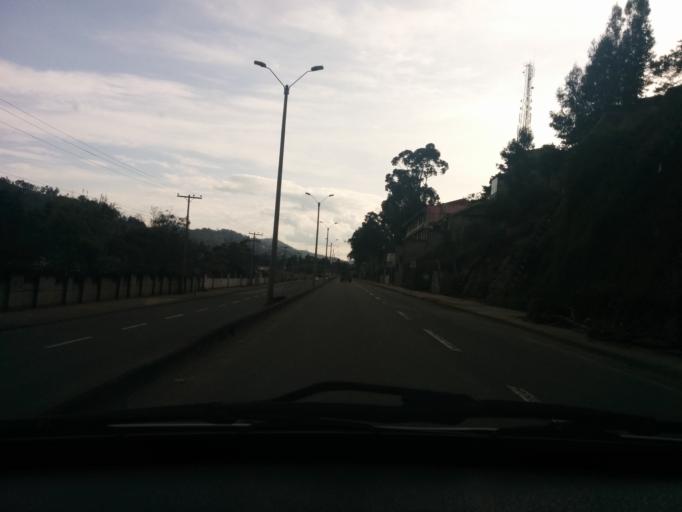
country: EC
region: Azuay
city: Cuenca
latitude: -2.8871
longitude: -78.9593
